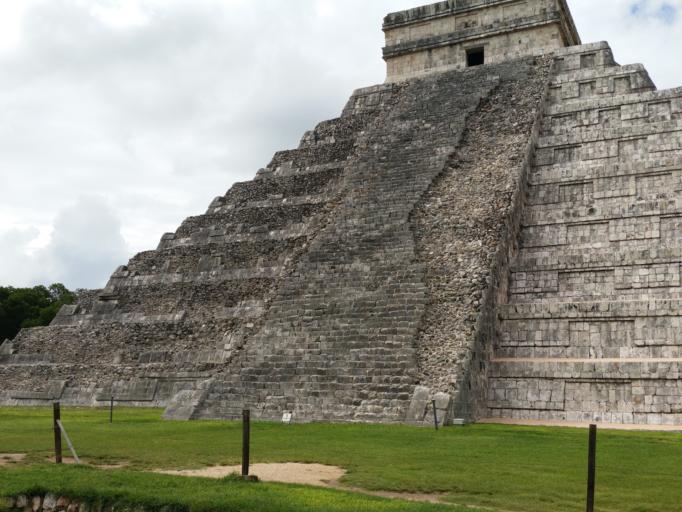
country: MX
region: Yucatan
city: Chichen-Itza
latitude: 20.6828
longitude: -88.5681
